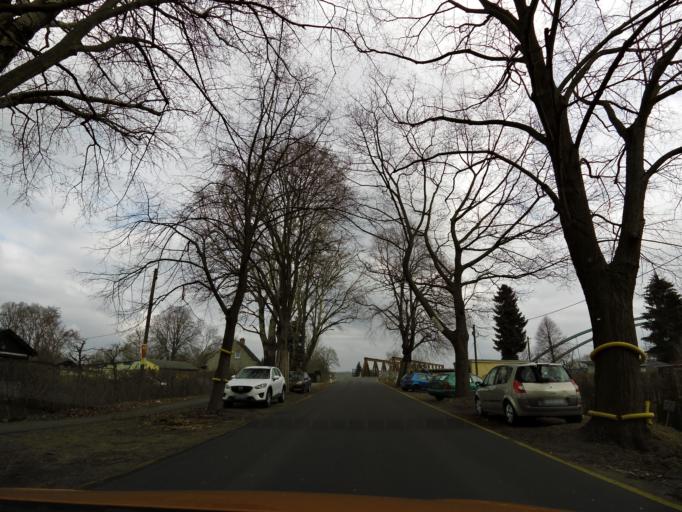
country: DE
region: Brandenburg
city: Werder
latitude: 52.4506
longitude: 12.9786
